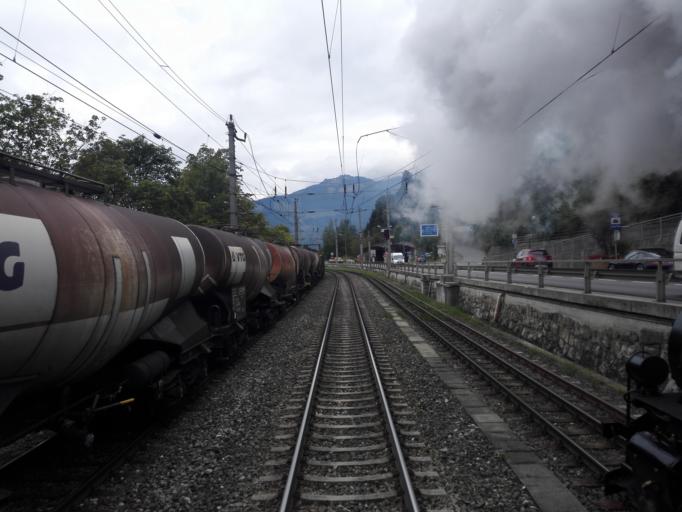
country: AT
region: Salzburg
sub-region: Politischer Bezirk Zell am See
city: Zell am See
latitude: 47.3148
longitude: 12.7942
